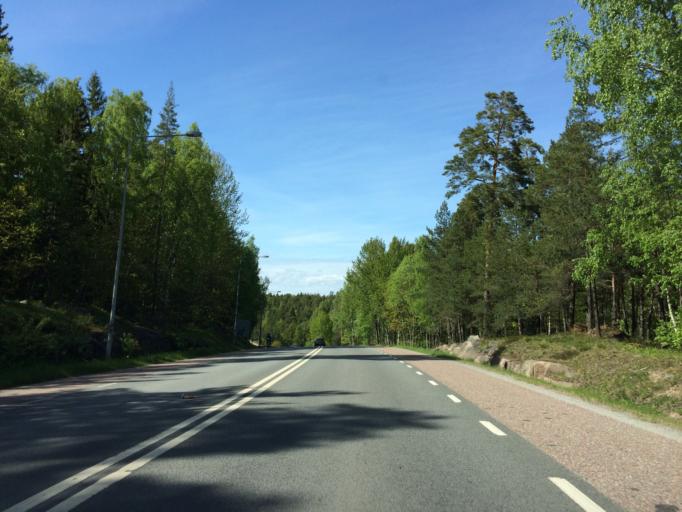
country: SE
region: Stockholm
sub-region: Sollentuna Kommun
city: Sollentuna
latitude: 59.4353
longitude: 17.9916
